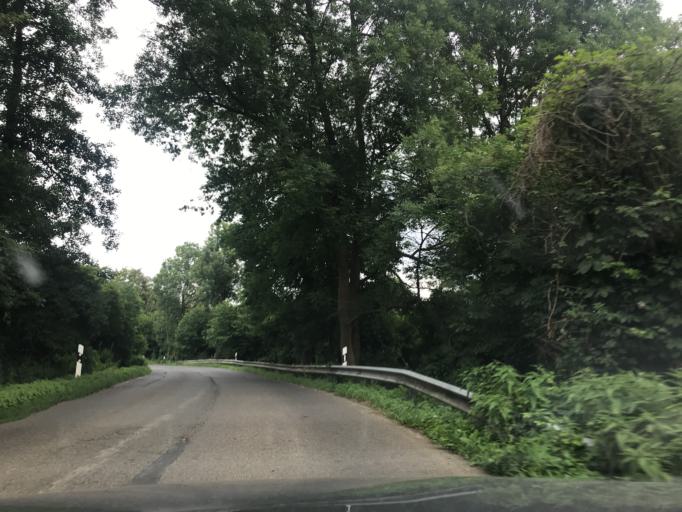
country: DE
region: North Rhine-Westphalia
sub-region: Regierungsbezirk Dusseldorf
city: Neubrueck
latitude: 51.1544
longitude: 6.6774
